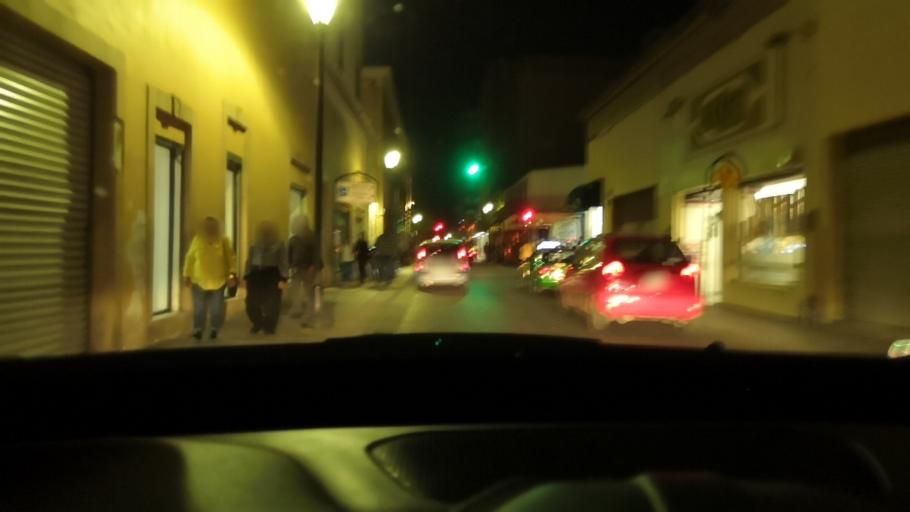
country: MX
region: Guanajuato
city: Leon
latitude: 21.1216
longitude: -101.6838
